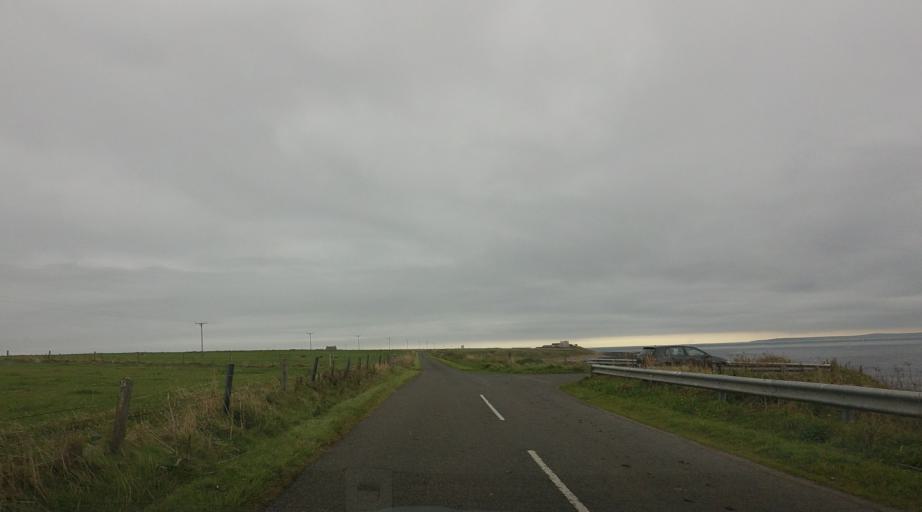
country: GB
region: Scotland
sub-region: Orkney Islands
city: Orkney
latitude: 58.7394
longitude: -2.9643
